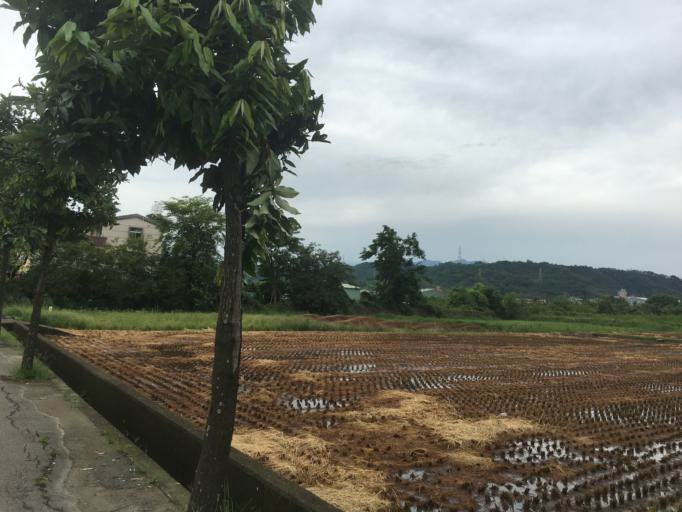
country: TW
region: Taiwan
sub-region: Taichung City
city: Taichung
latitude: 24.0543
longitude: 120.6871
